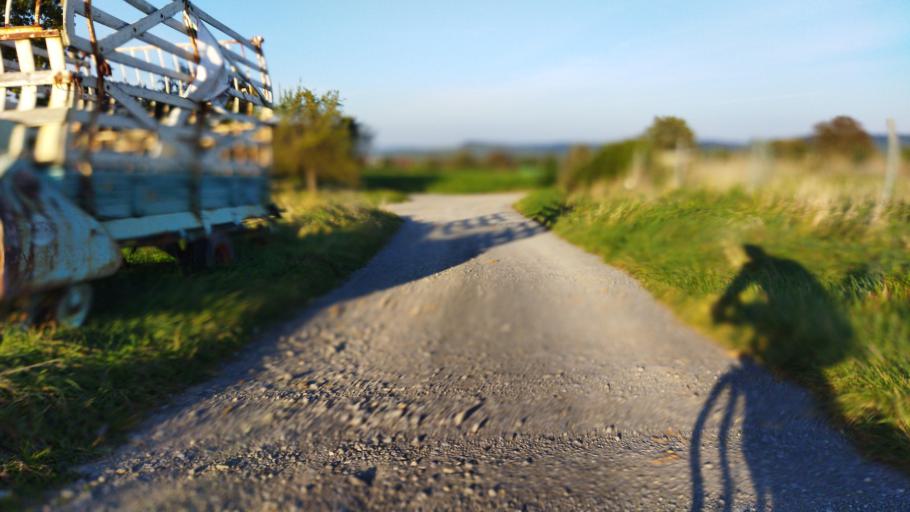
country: DE
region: Baden-Wuerttemberg
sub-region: Regierungsbezirk Stuttgart
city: Ilsfeld
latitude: 49.0374
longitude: 9.2698
